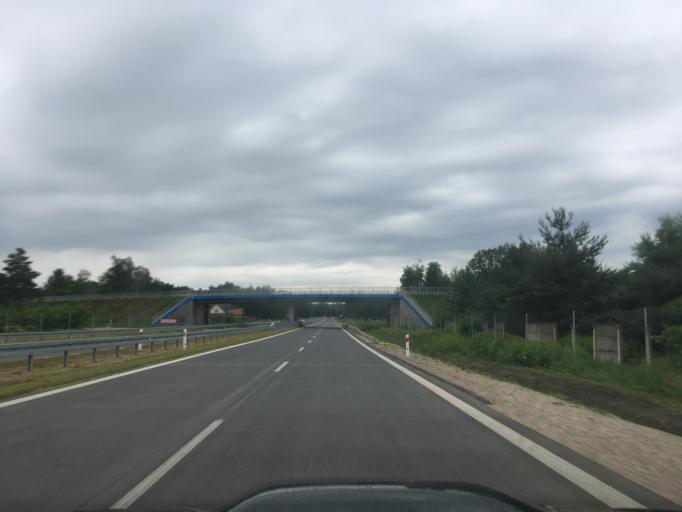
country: PL
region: Masovian Voivodeship
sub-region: Powiat piaseczynski
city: Gora Kalwaria
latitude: 51.9780
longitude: 21.1850
